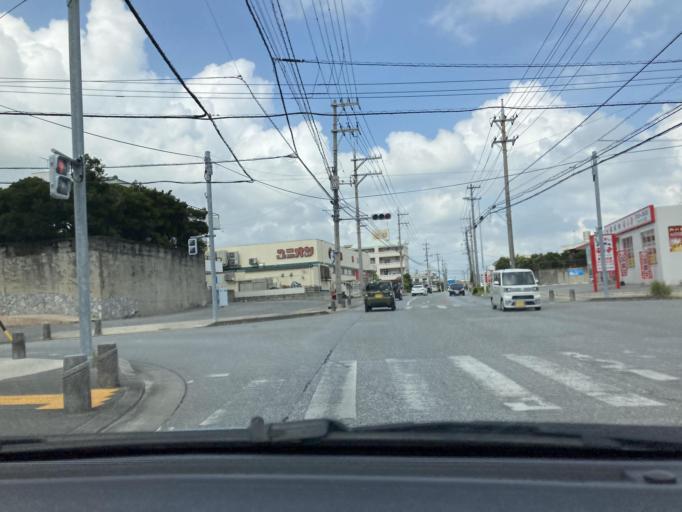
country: JP
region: Okinawa
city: Ginowan
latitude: 26.2522
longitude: 127.7725
